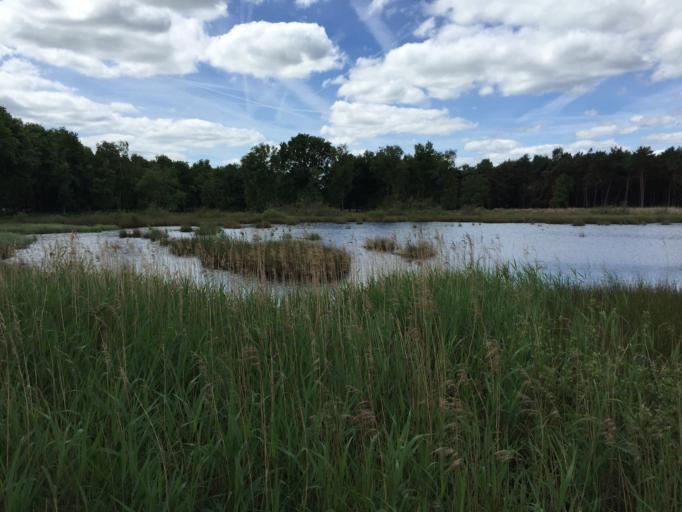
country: NL
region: Drenthe
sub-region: Gemeente Assen
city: Assen
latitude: 52.9100
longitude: 6.4871
